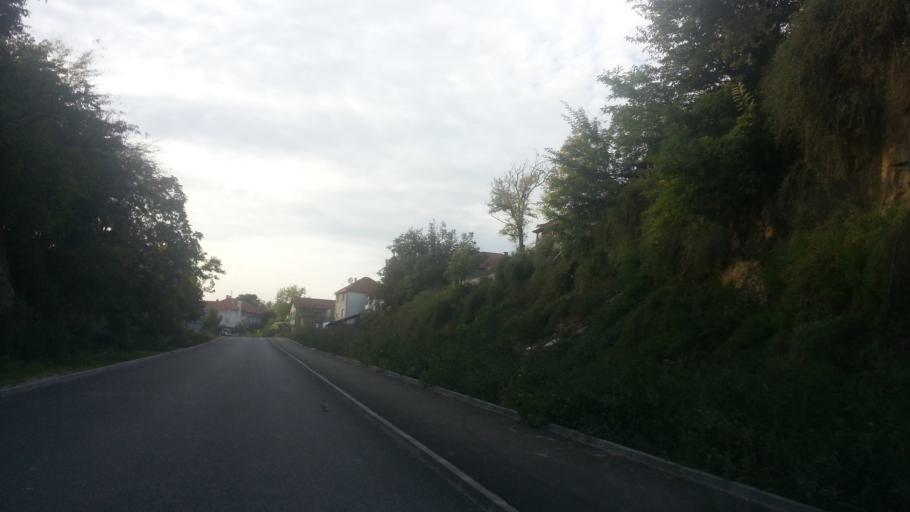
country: RS
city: Belegis
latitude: 45.0178
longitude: 20.3364
